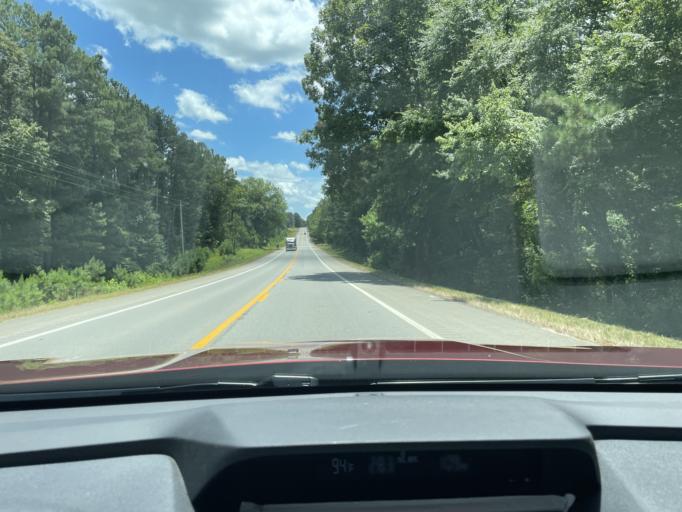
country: US
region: Arkansas
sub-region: Drew County
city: Monticello
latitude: 33.7371
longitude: -91.8183
